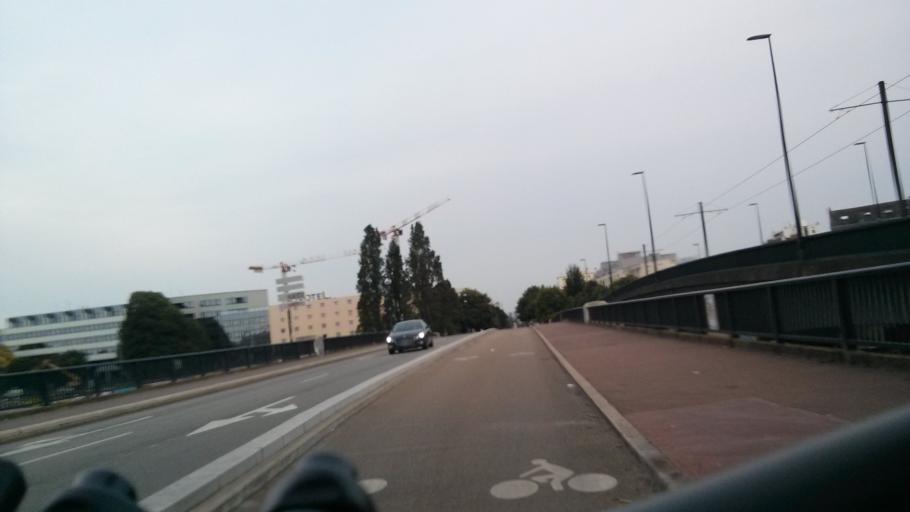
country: FR
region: Pays de la Loire
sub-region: Departement de la Loire-Atlantique
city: Nantes
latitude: 47.2086
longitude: -1.5496
